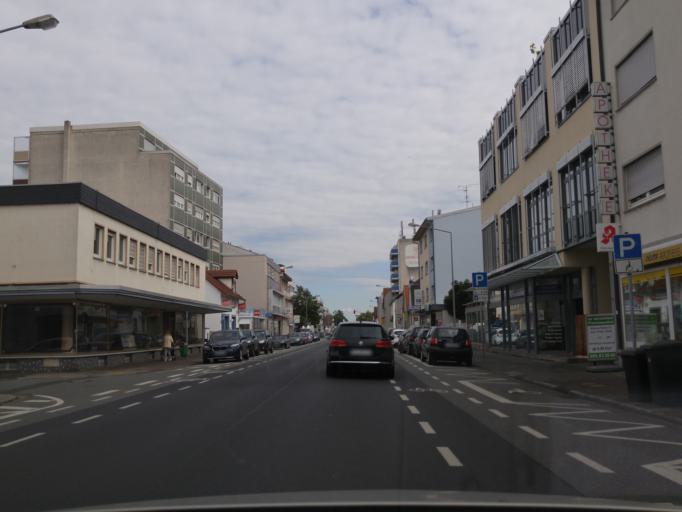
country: DE
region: Hesse
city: Dreieich
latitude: 50.0221
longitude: 8.6955
